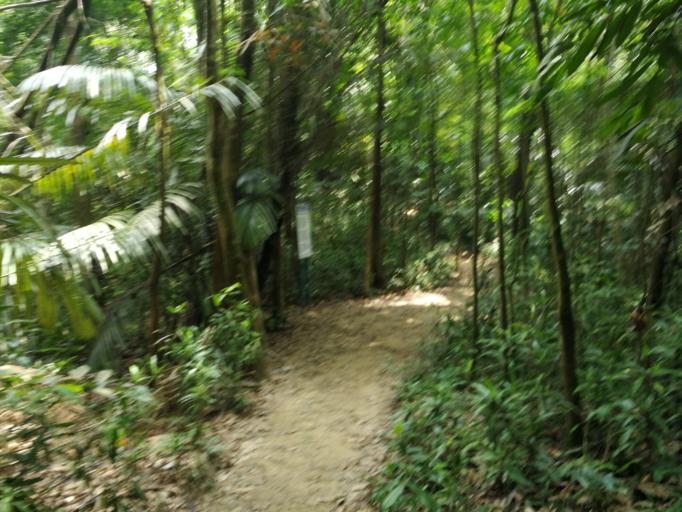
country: MY
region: Kuala Lumpur
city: Kuala Lumpur
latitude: 3.1001
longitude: 101.6585
